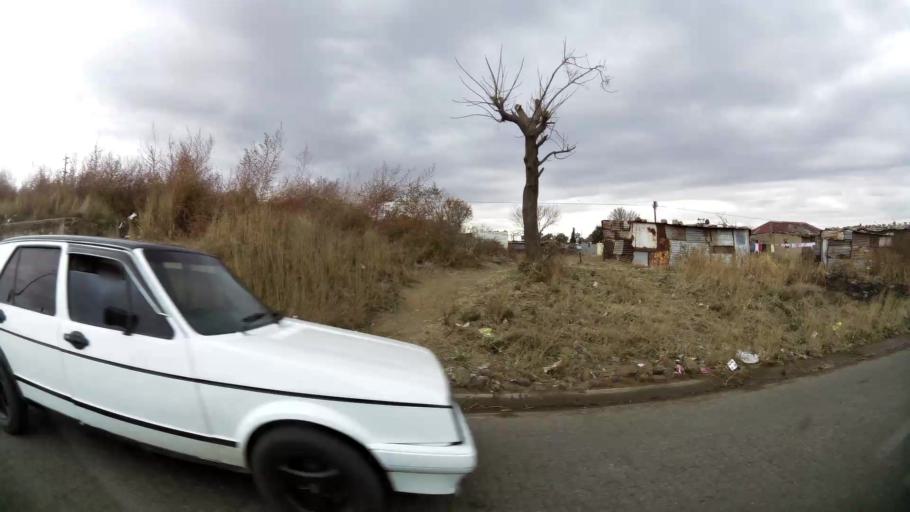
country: ZA
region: Orange Free State
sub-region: Fezile Dabi District Municipality
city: Kroonstad
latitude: -27.6519
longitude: 27.2223
